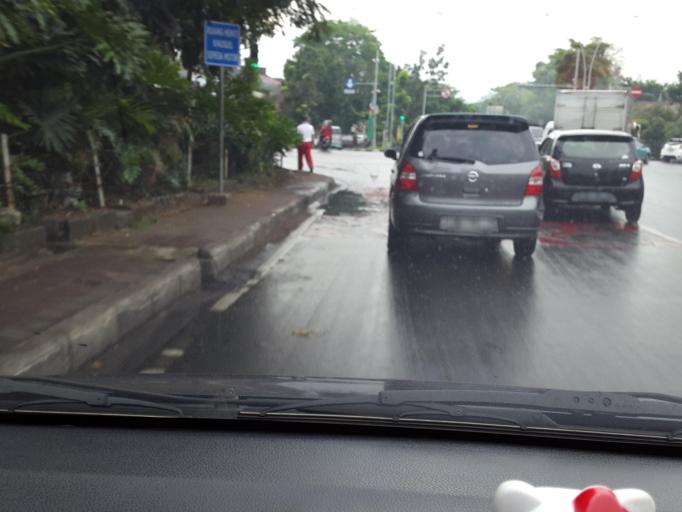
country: ID
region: West Java
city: Bandung
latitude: -6.8983
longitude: 107.6340
